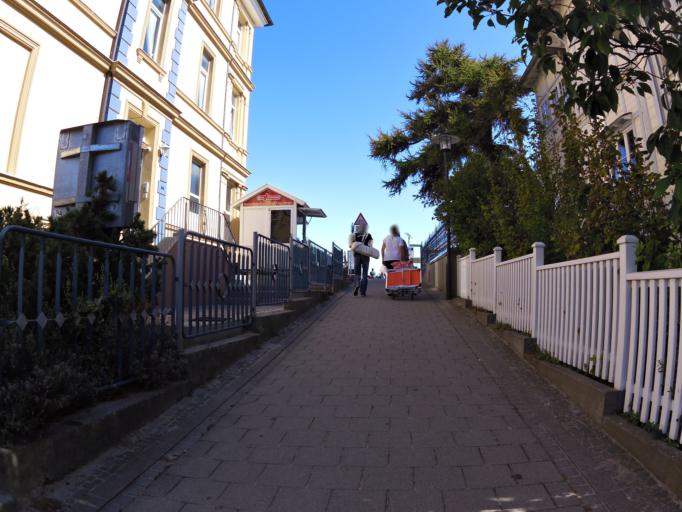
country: DE
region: Mecklenburg-Vorpommern
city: Seebad Bansin
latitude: 53.9714
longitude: 14.1463
